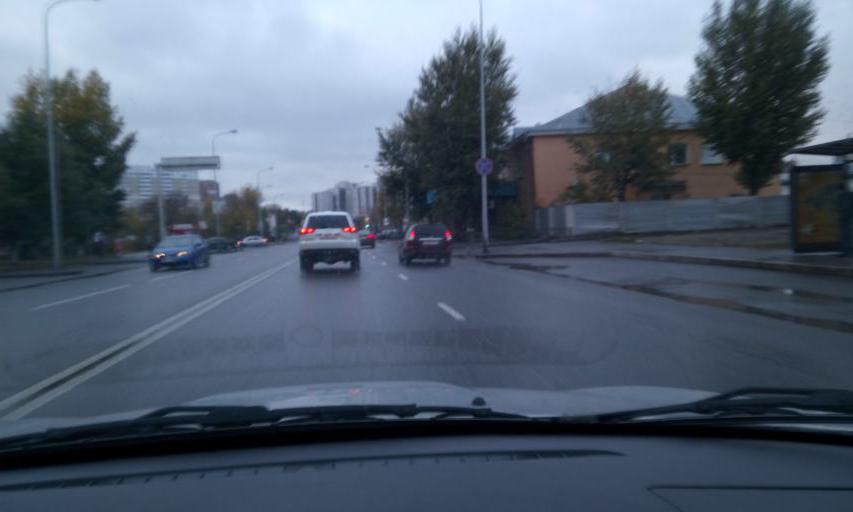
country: KZ
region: Astana Qalasy
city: Astana
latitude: 51.1631
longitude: 71.4523
